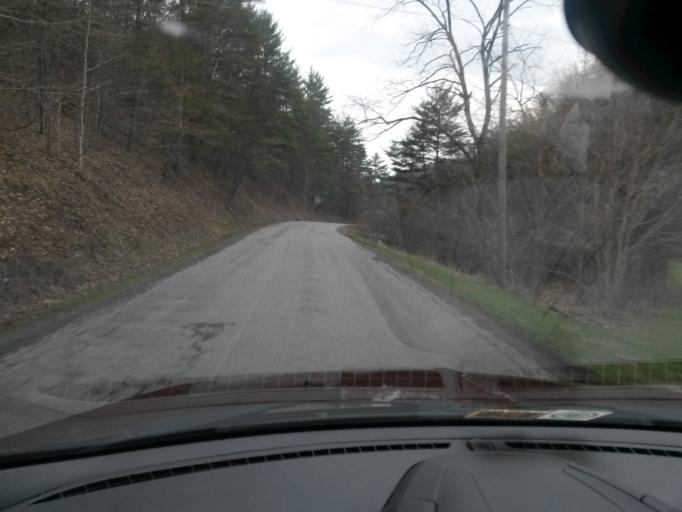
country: US
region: Virginia
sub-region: Bath County
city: Warm Springs
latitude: 38.0172
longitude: -79.8695
